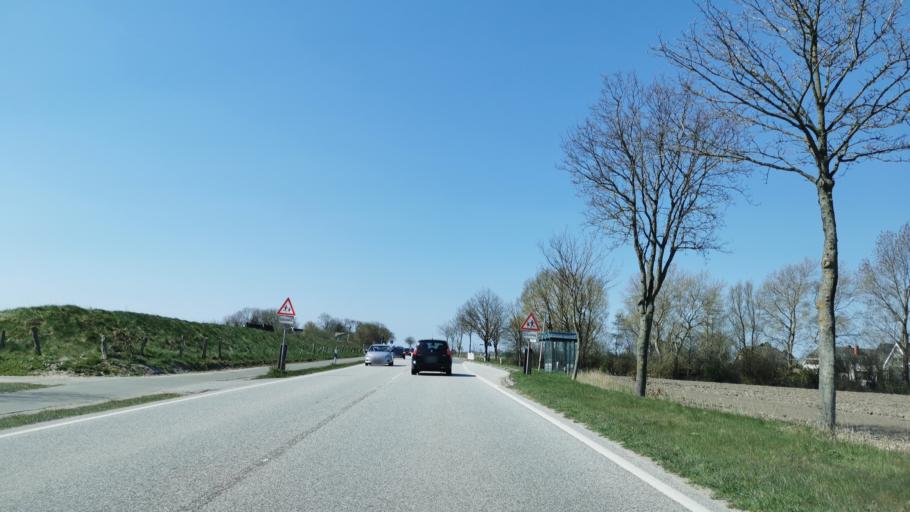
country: DE
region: Schleswig-Holstein
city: Oesterdeichstrich
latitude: 54.1590
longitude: 8.8928
